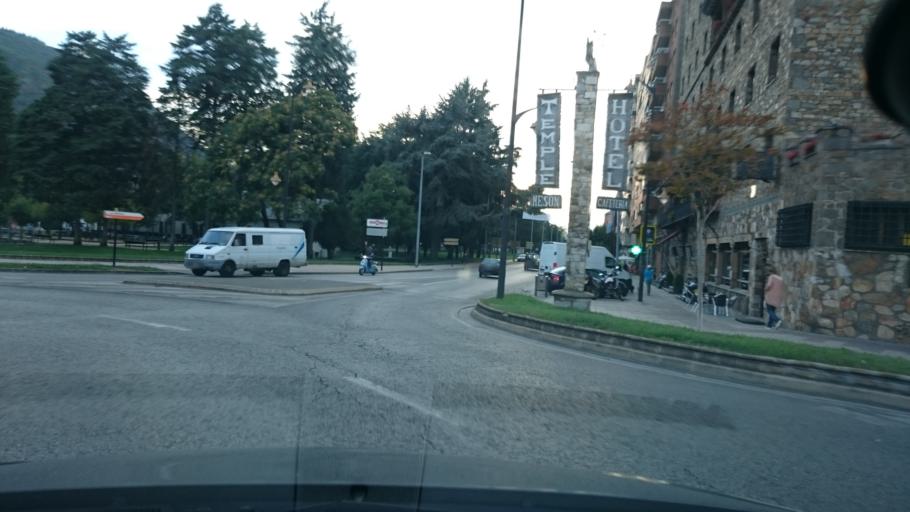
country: ES
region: Castille and Leon
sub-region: Provincia de Leon
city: Ponferrada
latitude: 42.5470
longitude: -6.6049
